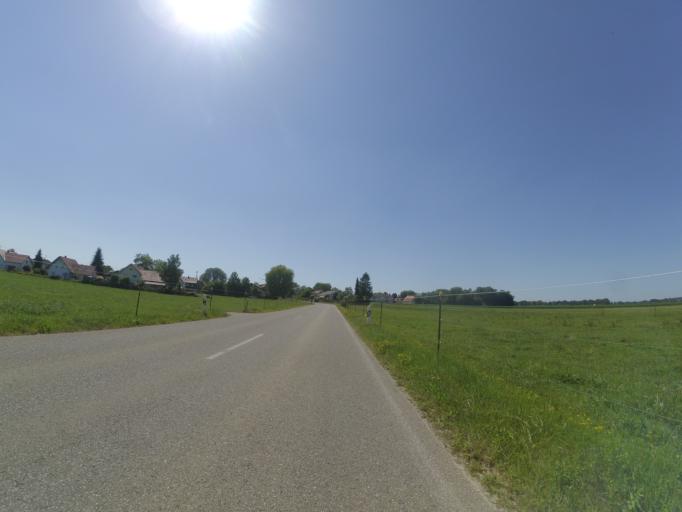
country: DE
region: Bavaria
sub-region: Swabia
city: Benningen
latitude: 47.9688
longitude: 10.2176
